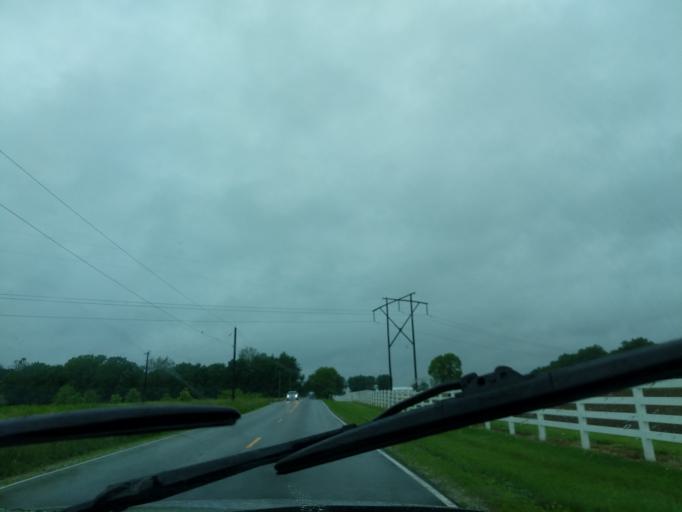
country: US
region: Indiana
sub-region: Hamilton County
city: Noblesville
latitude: 40.0661
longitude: -85.9496
